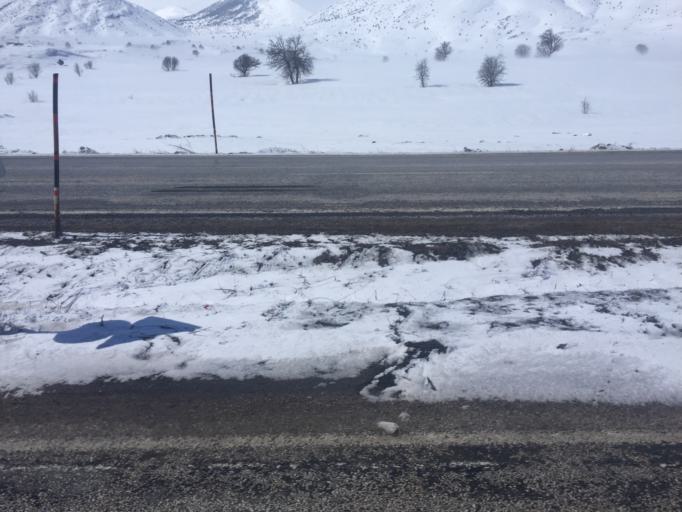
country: TR
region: Kahramanmaras
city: Goksun
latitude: 38.1740
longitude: 36.4615
